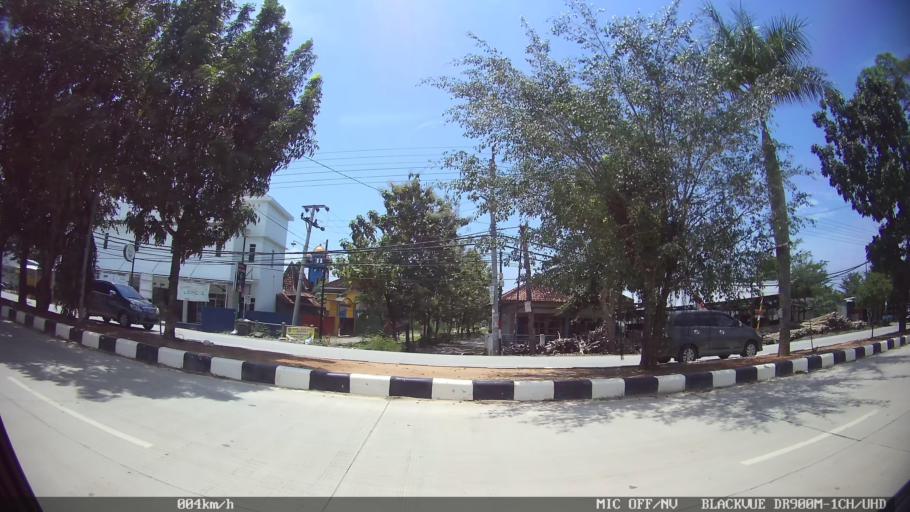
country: ID
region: Lampung
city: Kedaton
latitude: -5.3749
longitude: 105.2957
